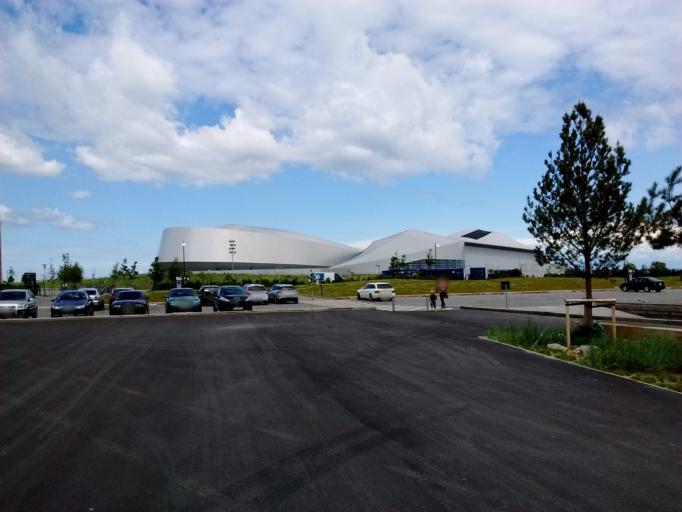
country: DK
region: Capital Region
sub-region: Dragor Kommune
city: Dragor
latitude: 55.6366
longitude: 12.6550
